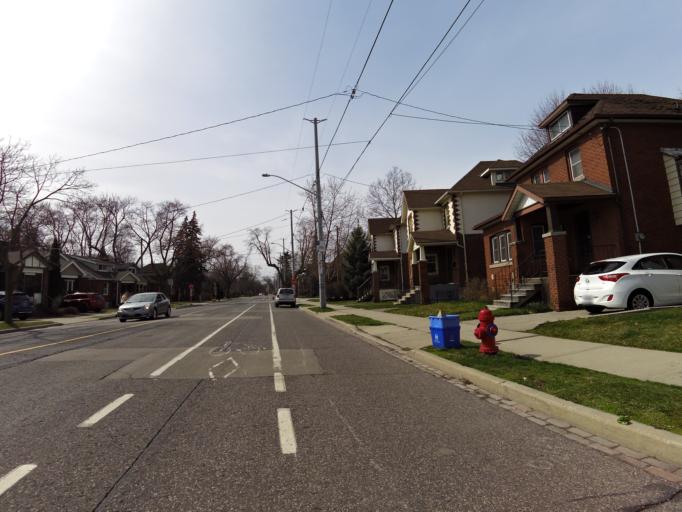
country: CA
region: Ontario
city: Hamilton
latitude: 43.2620
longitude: -79.9093
